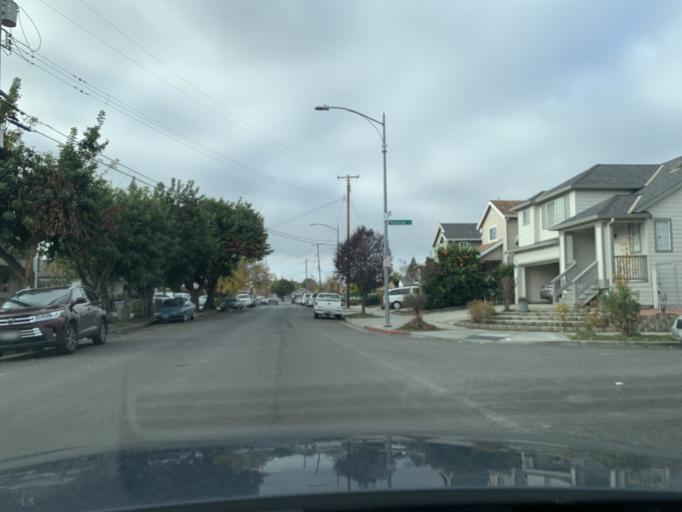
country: US
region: California
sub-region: Santa Clara County
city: Alum Rock
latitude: 37.3319
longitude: -121.8501
